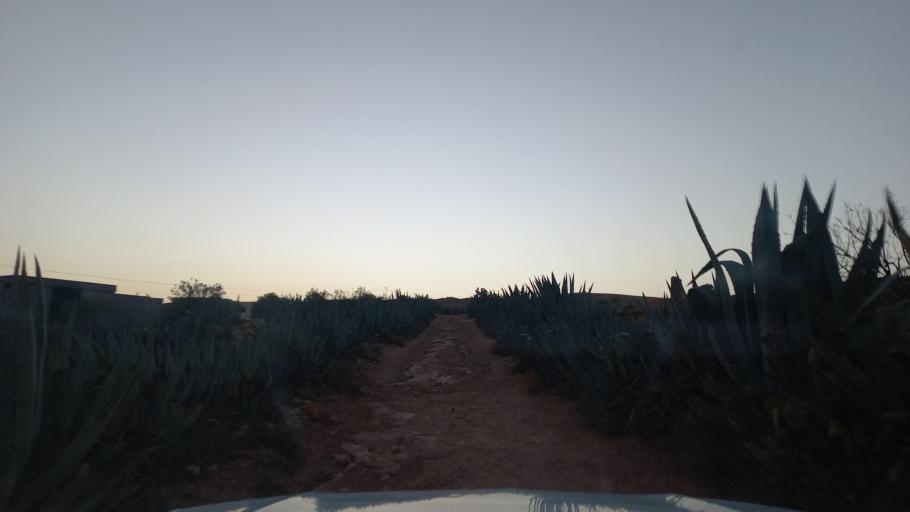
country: TN
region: Al Qasrayn
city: Sbiba
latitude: 35.3773
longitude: 9.0131
